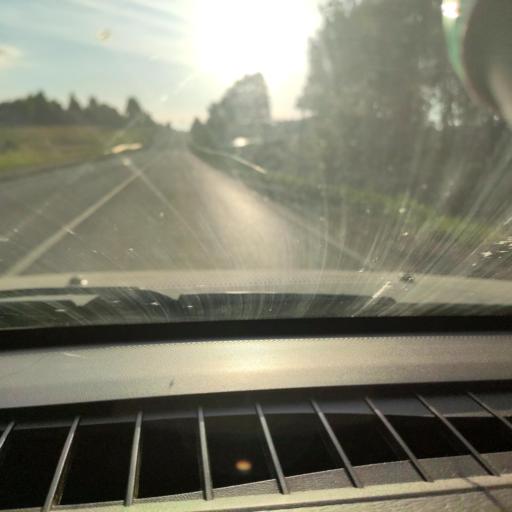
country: RU
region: Kirov
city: Belaya Kholunitsa
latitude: 58.8430
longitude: 50.7002
